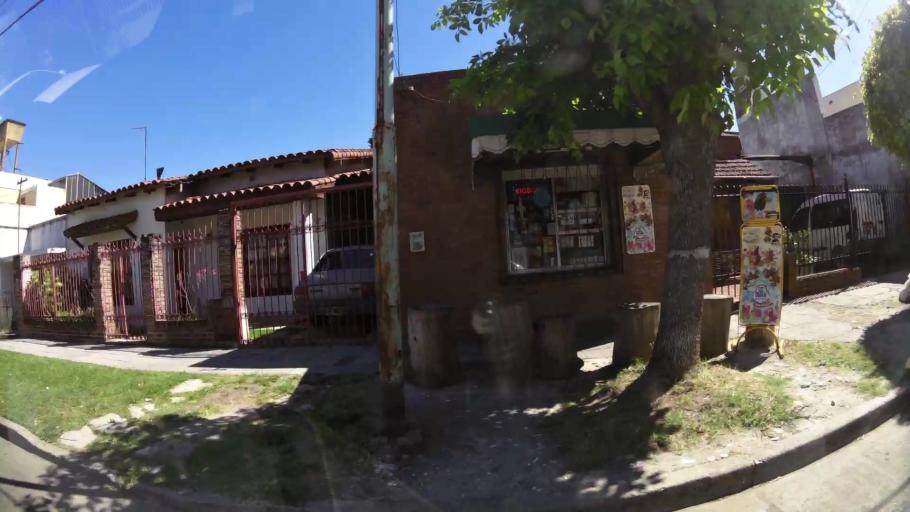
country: AR
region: Buenos Aires
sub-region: Partido de General San Martin
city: General San Martin
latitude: -34.5295
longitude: -58.5610
